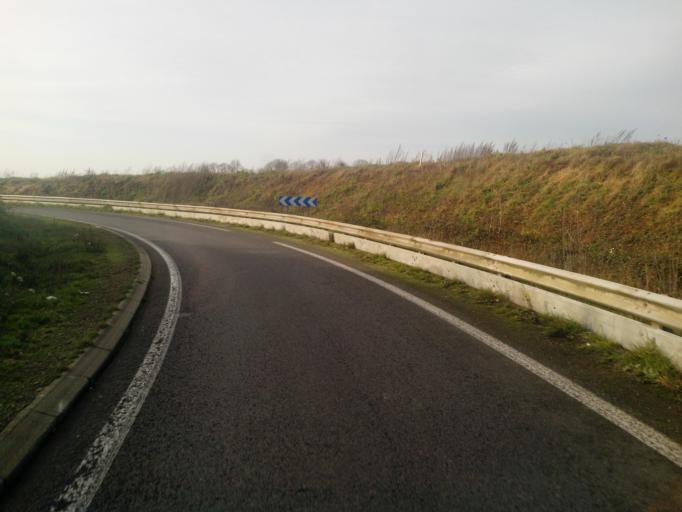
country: FR
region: Brittany
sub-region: Departement d'Ille-et-Vilaine
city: Montauban-de-Bretagne
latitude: 48.2097
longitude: -2.0728
